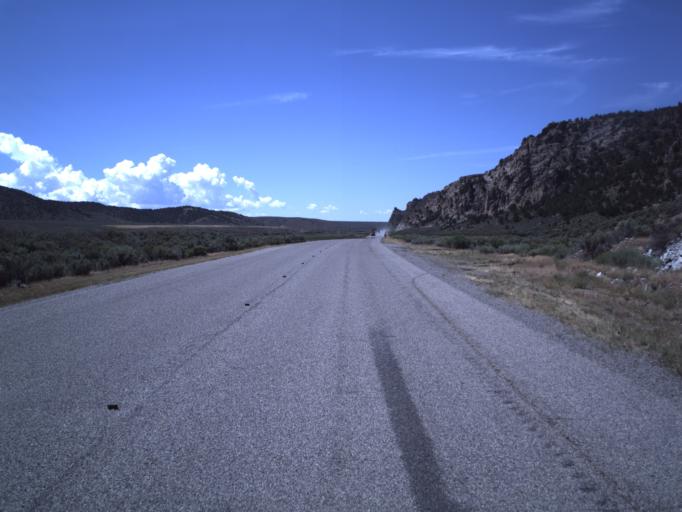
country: US
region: Utah
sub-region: Piute County
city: Junction
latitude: 38.0456
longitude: -112.3539
